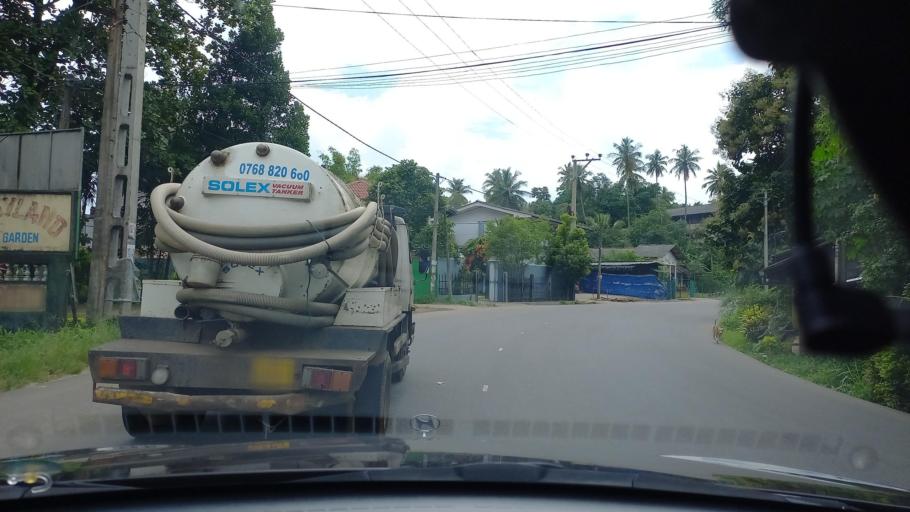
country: LK
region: Central
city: Kadugannawa
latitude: 7.2470
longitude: 80.4650
